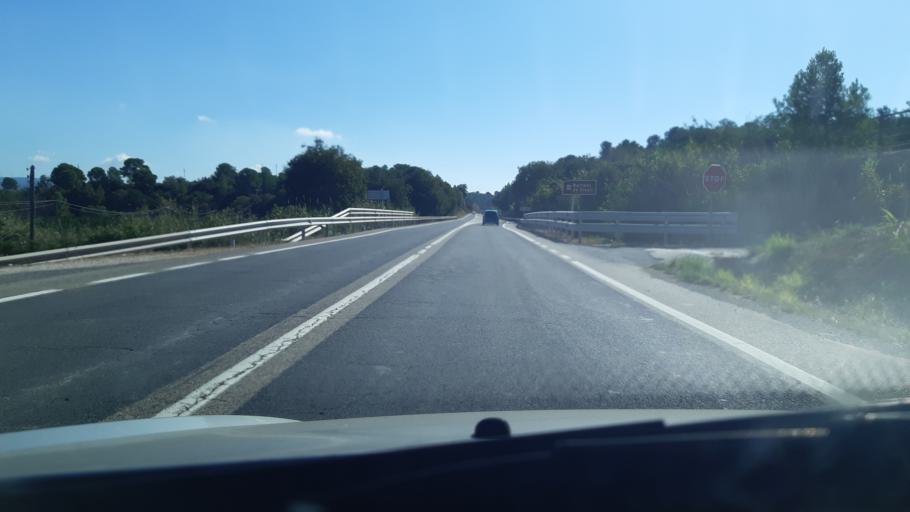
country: ES
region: Catalonia
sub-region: Provincia de Tarragona
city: Tivenys
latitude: 40.8916
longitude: 0.4900
